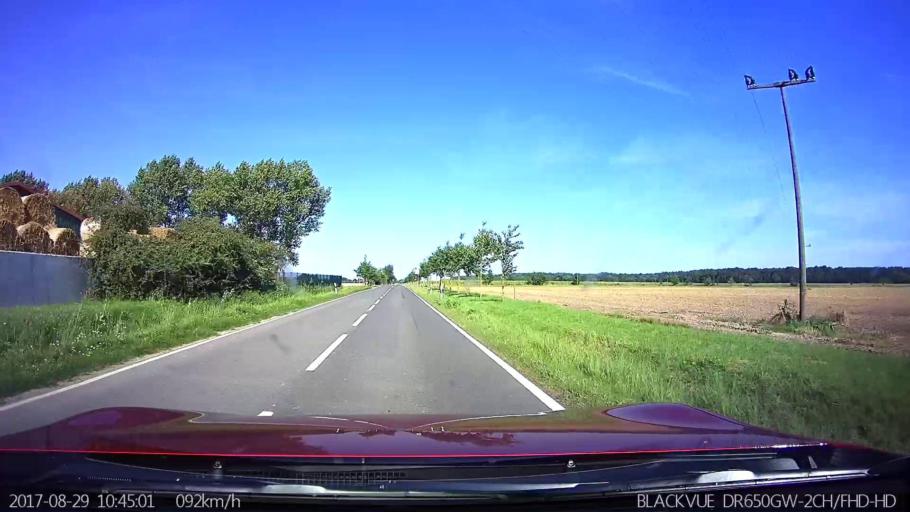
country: DE
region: Mecklenburg-Vorpommern
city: Richtenberg
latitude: 54.2086
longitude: 12.8692
